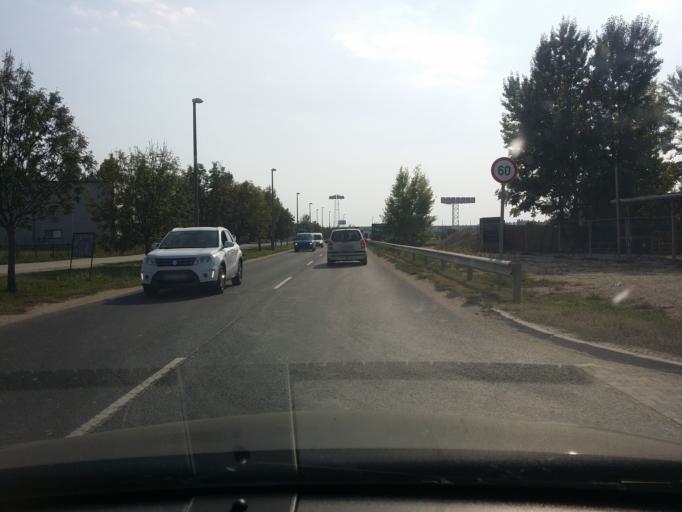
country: HU
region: Pest
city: Dunakeszi
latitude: 47.6150
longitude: 19.1181
